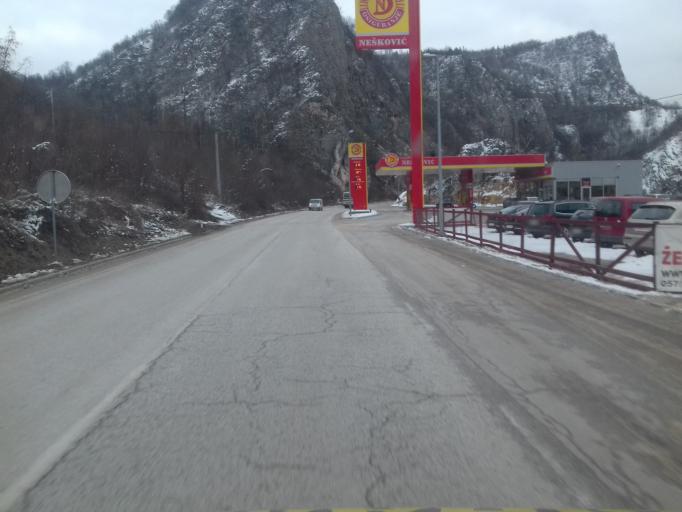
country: BA
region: Republika Srpska
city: Pale
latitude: 43.8497
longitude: 18.5107
